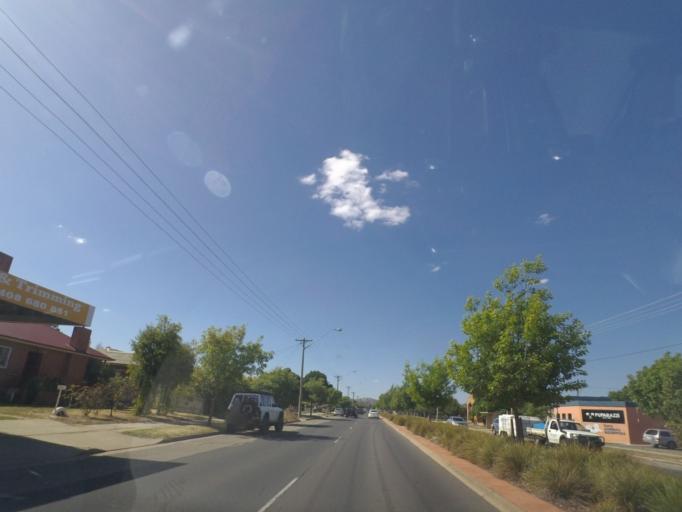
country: AU
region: New South Wales
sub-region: Albury Municipality
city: North Albury
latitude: -36.0593
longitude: 146.9323
